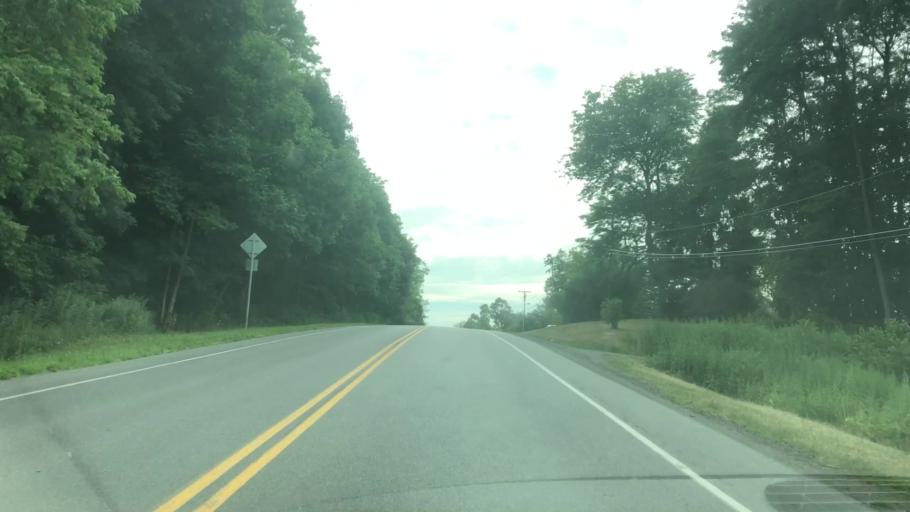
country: US
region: New York
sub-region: Wayne County
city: Macedon
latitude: 43.1349
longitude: -77.3575
